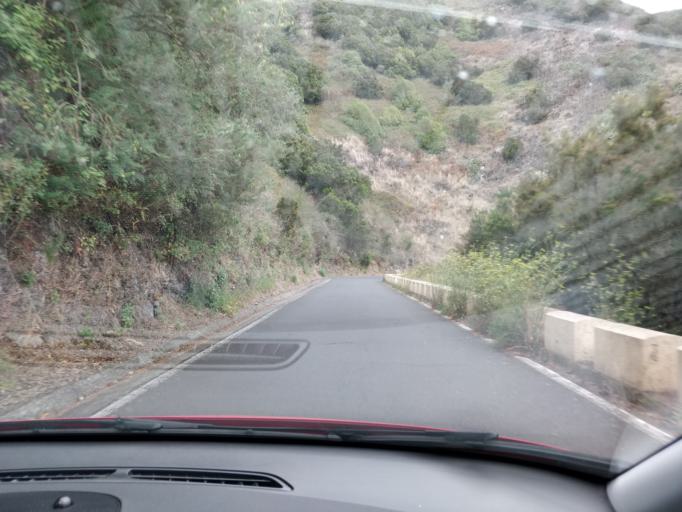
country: ES
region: Canary Islands
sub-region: Provincia de Santa Cruz de Tenerife
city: Santiago del Teide
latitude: 28.3240
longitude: -16.8512
